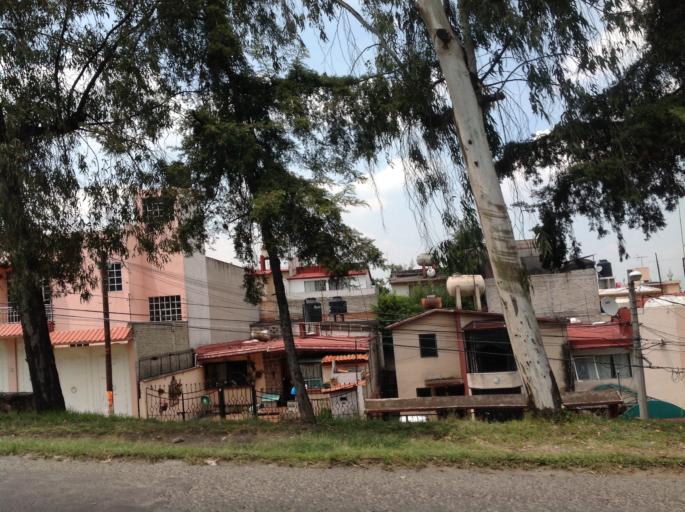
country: MX
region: Mexico
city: Ciudad Lopez Mateos
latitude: 19.5941
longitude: -99.2299
